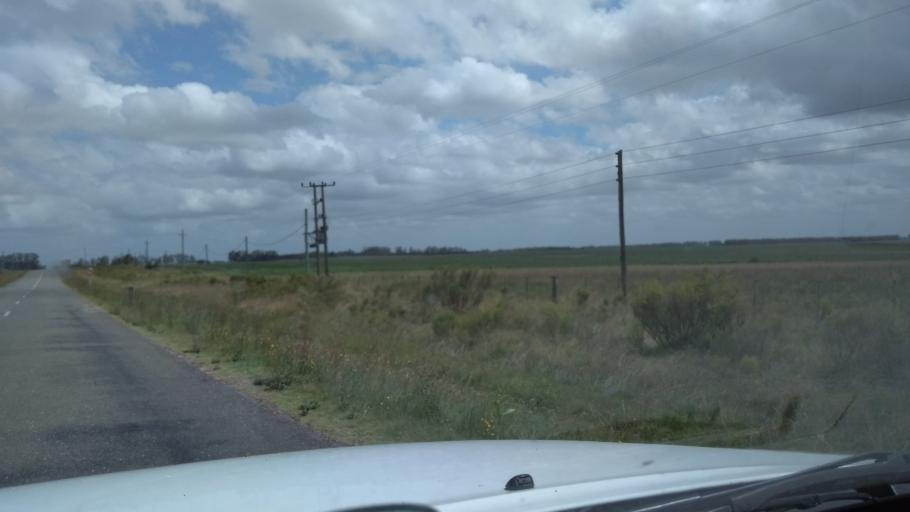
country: UY
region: Canelones
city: San Ramon
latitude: -34.1164
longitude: -55.9424
